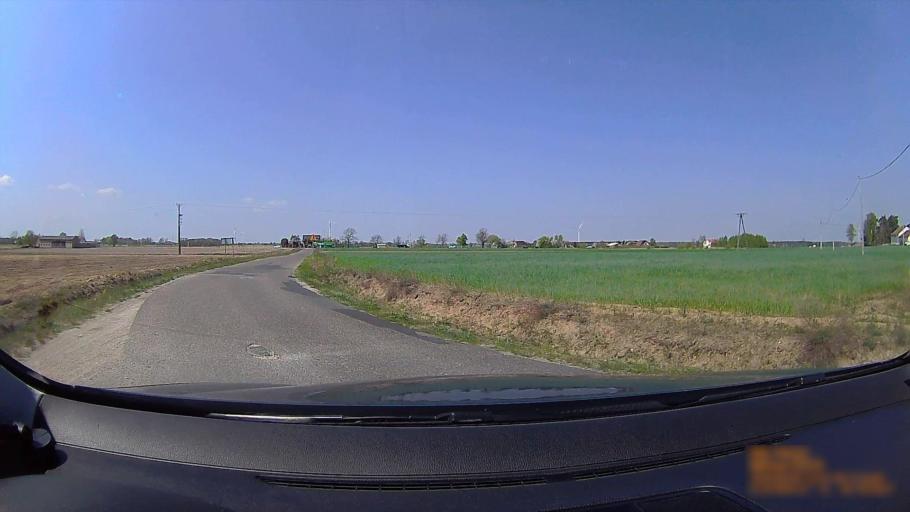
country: PL
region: Greater Poland Voivodeship
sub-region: Powiat koninski
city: Rychwal
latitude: 52.1026
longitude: 18.1719
